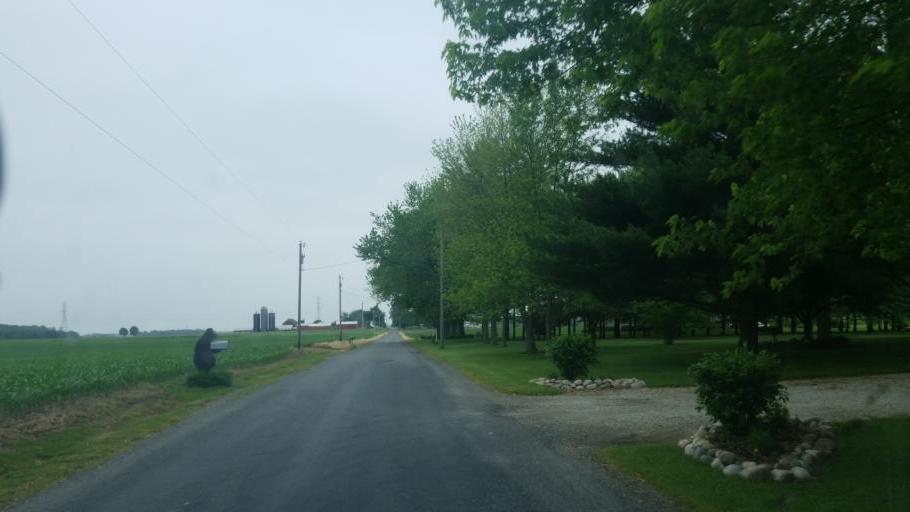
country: US
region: Indiana
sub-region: Marshall County
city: Bremen
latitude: 41.4938
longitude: -86.1313
